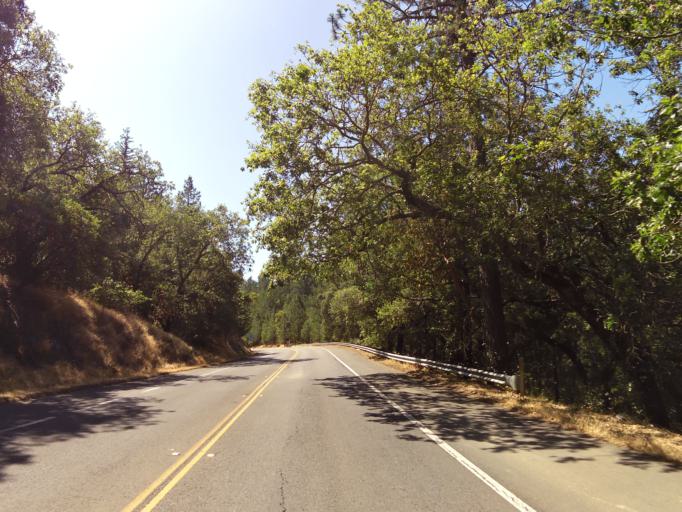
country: US
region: California
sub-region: Napa County
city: Deer Park
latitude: 38.5522
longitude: -122.4980
